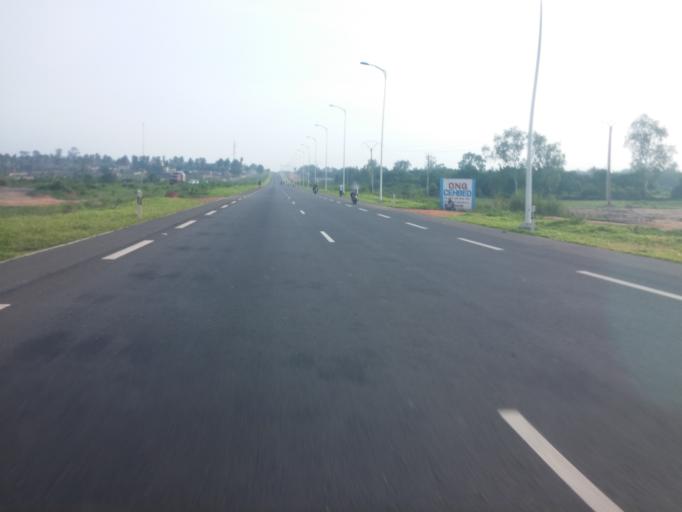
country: TG
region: Maritime
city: Tsevie
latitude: 6.3102
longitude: 1.2162
